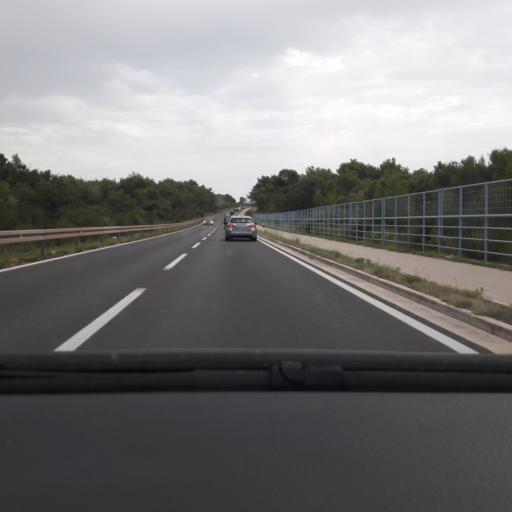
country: HR
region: Zadarska
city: Nin
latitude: 44.1829
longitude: 15.1861
